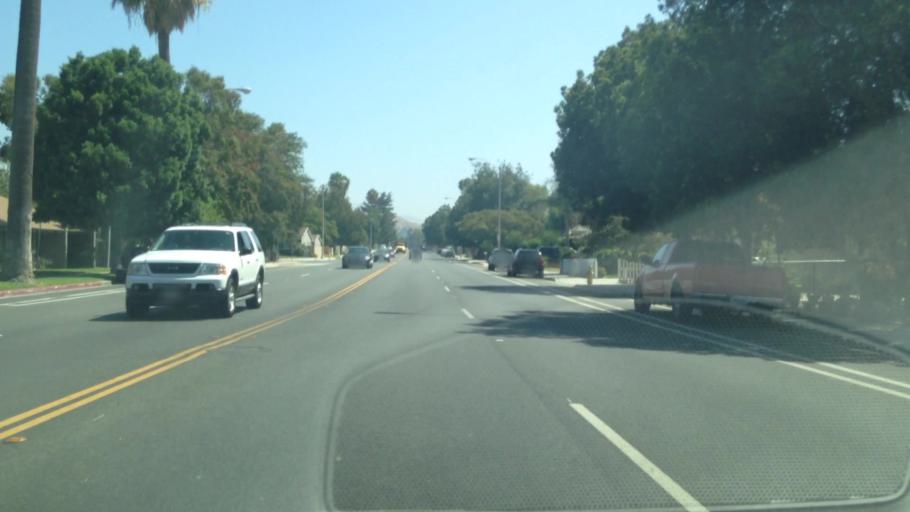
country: US
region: California
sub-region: Riverside County
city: Riverside
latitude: 33.9614
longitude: -117.4072
